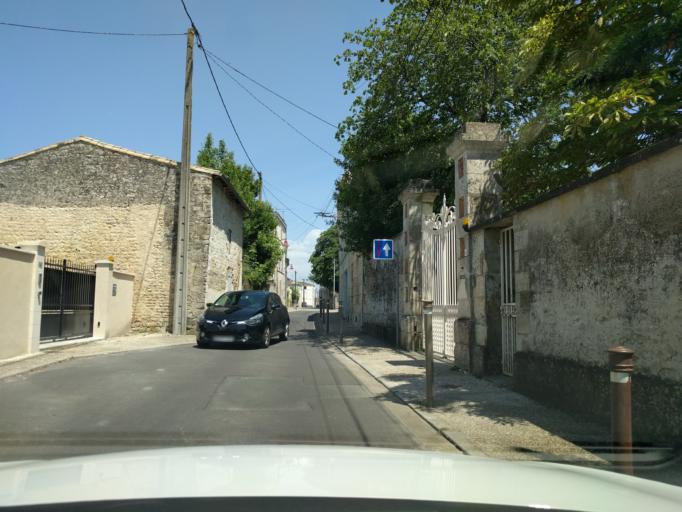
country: FR
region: Poitou-Charentes
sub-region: Departement des Deux-Sevres
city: Niort
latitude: 46.3483
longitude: -0.4705
